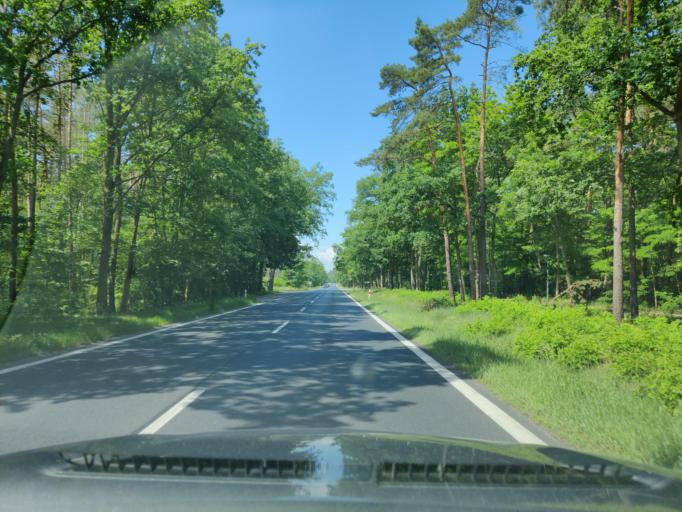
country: PL
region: Greater Poland Voivodeship
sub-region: Powiat grodziski
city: Rakoniewice
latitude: 52.1345
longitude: 16.2429
